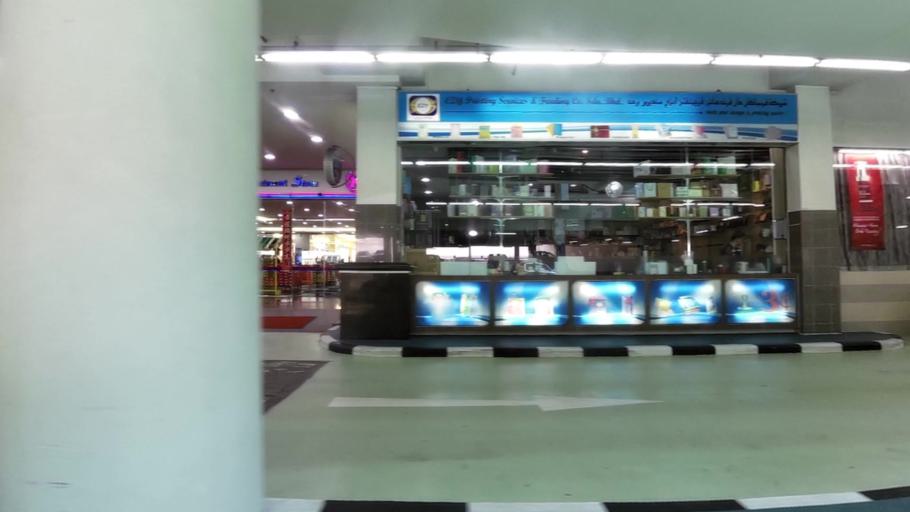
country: BN
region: Brunei and Muara
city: Bandar Seri Begawan
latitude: 4.9473
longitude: 114.9606
